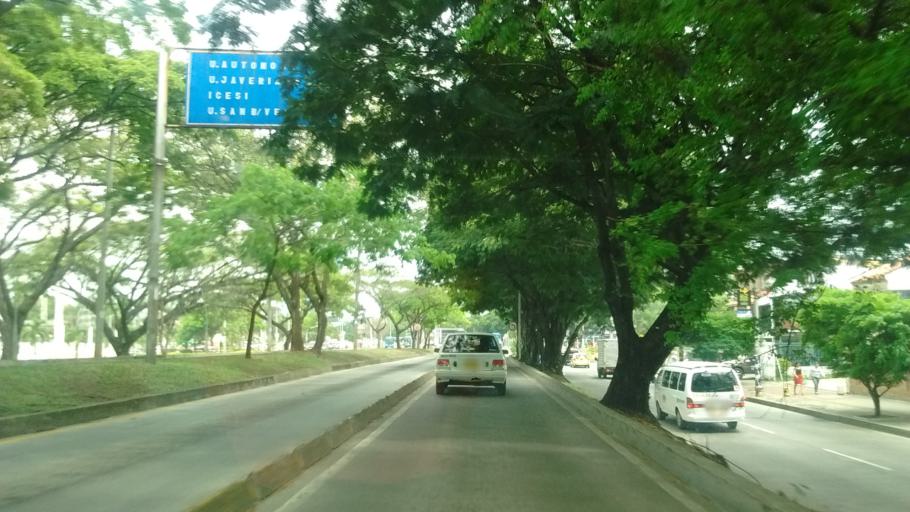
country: CO
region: Valle del Cauca
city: Cali
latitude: 3.3679
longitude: -76.5309
